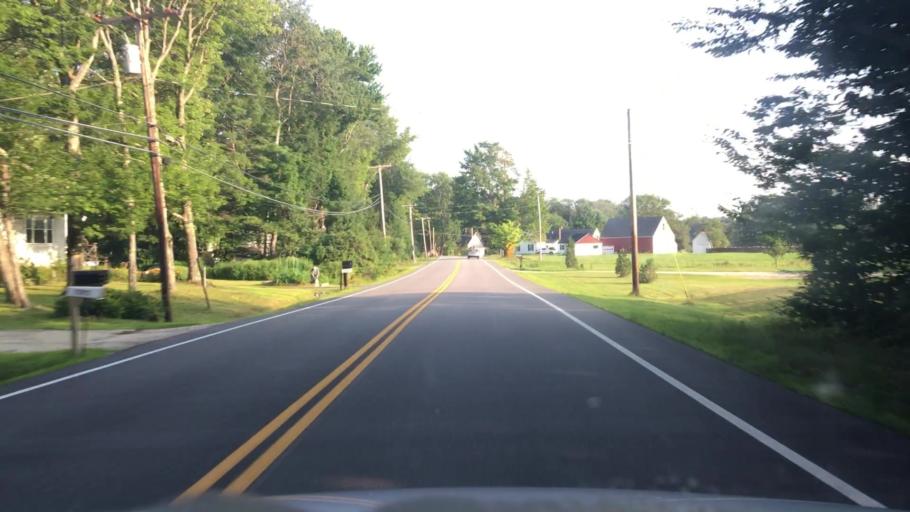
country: US
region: Maine
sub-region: Cumberland County
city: Freeport
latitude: 43.8837
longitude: -70.0932
